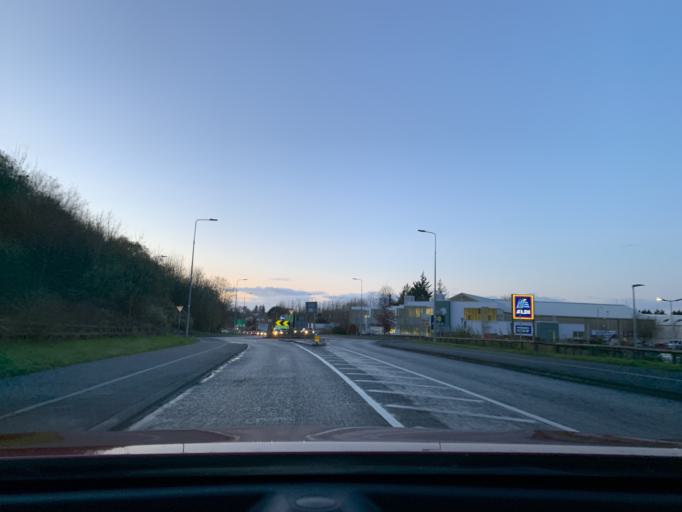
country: IE
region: Connaught
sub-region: County Leitrim
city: Carrick-on-Shannon
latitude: 53.9450
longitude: -8.0742
